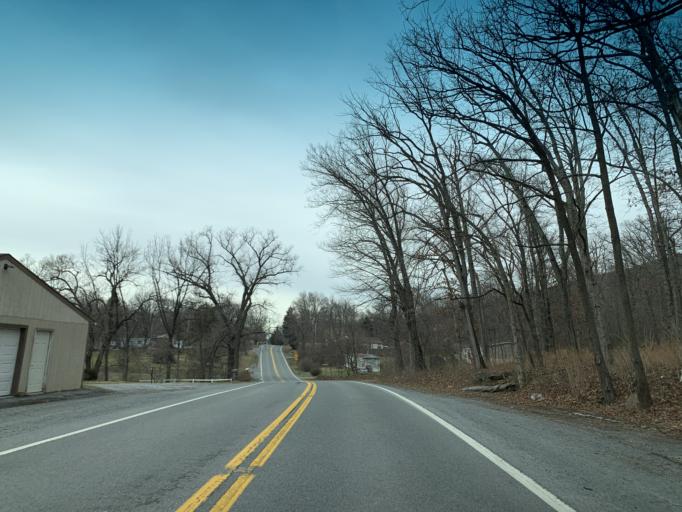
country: US
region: West Virginia
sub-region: Jefferson County
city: Shannondale
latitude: 39.2484
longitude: -77.7803
